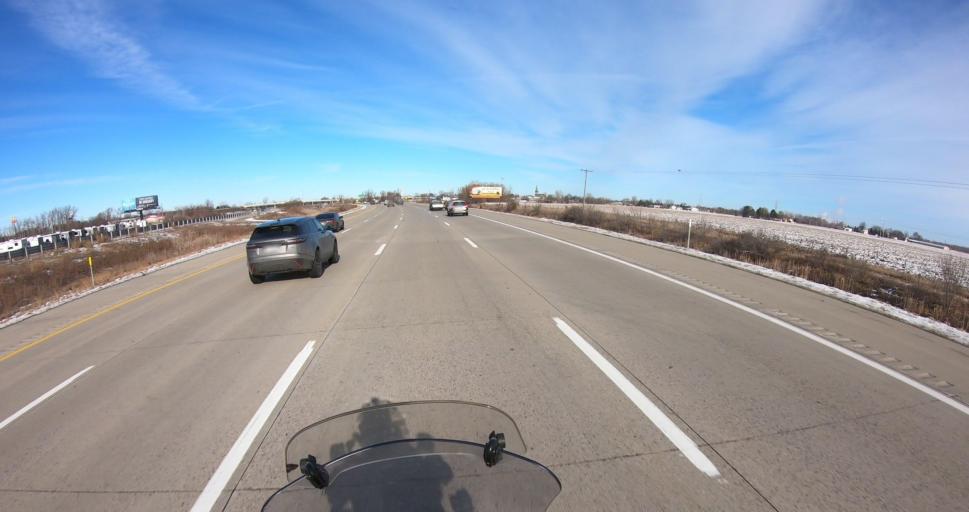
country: US
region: Michigan
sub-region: Bay County
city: Bay City
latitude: 43.5538
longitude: -83.9443
